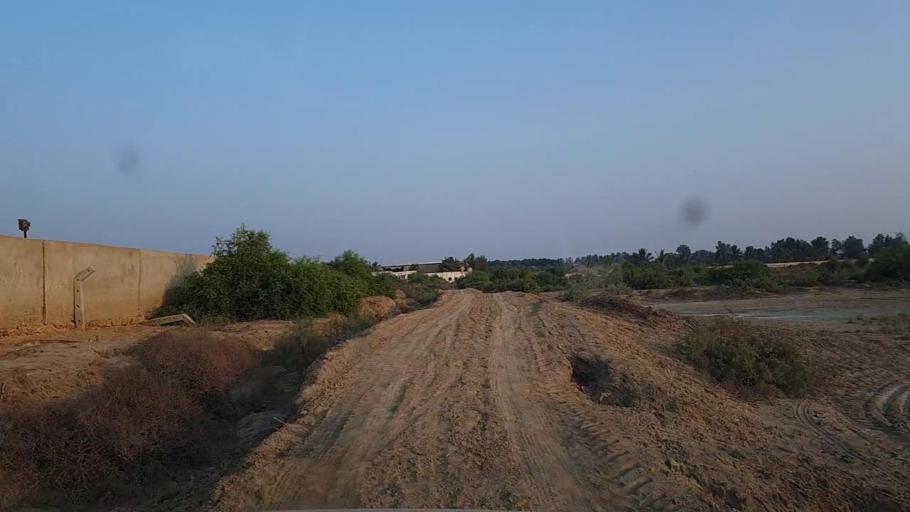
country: PK
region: Sindh
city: Mirpur Sakro
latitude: 24.6137
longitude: 67.5920
